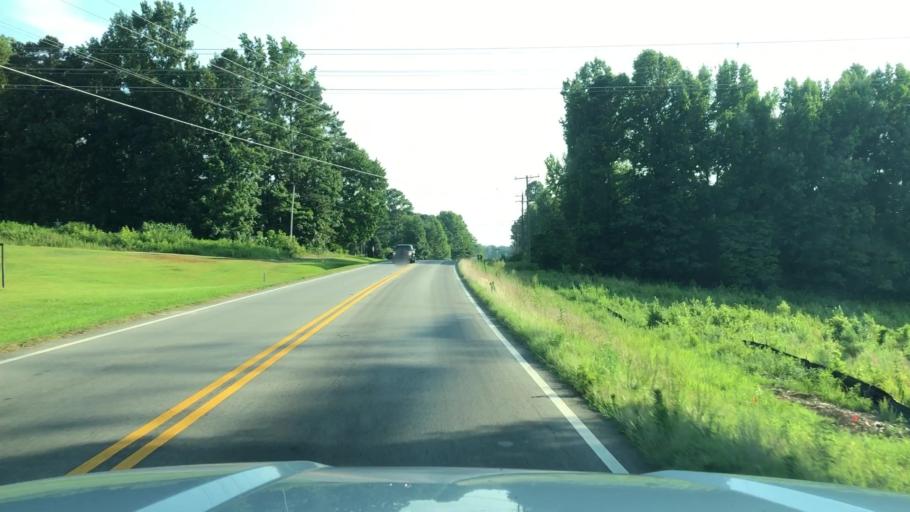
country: US
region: Georgia
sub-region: Bartow County
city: Emerson
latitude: 34.0458
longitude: -84.8352
